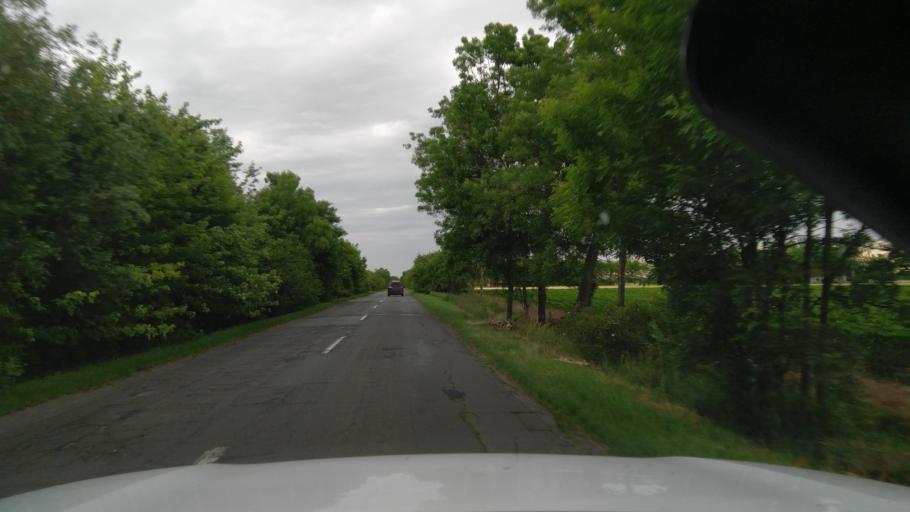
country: HU
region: Bekes
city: Bekescsaba
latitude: 46.6866
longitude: 21.1670
